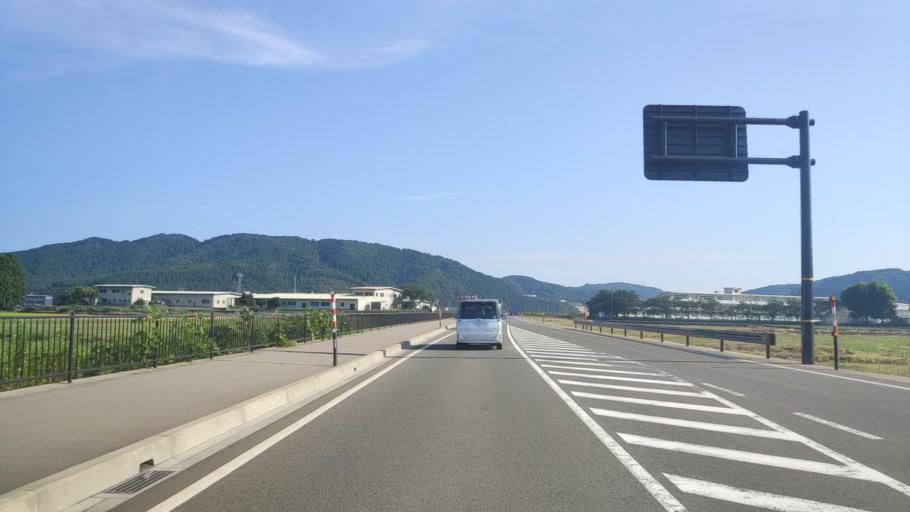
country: JP
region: Fukui
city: Maruoka
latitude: 36.1943
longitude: 136.2677
